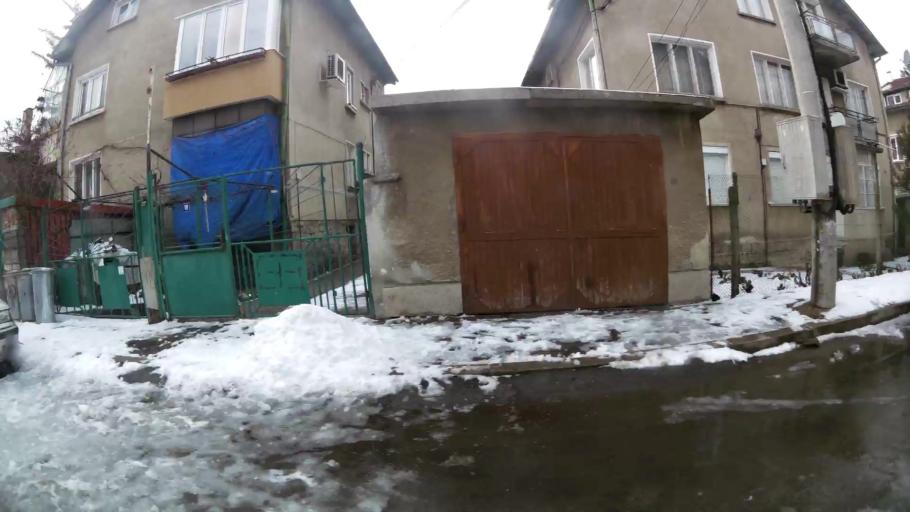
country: BG
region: Sofia-Capital
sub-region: Stolichna Obshtina
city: Sofia
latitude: 42.7002
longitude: 23.3801
